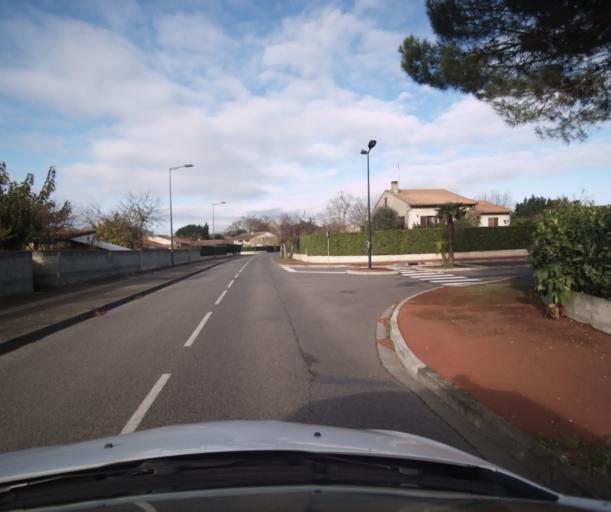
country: FR
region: Midi-Pyrenees
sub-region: Departement de la Haute-Garonne
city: Bruguieres
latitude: 43.7231
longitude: 1.4152
